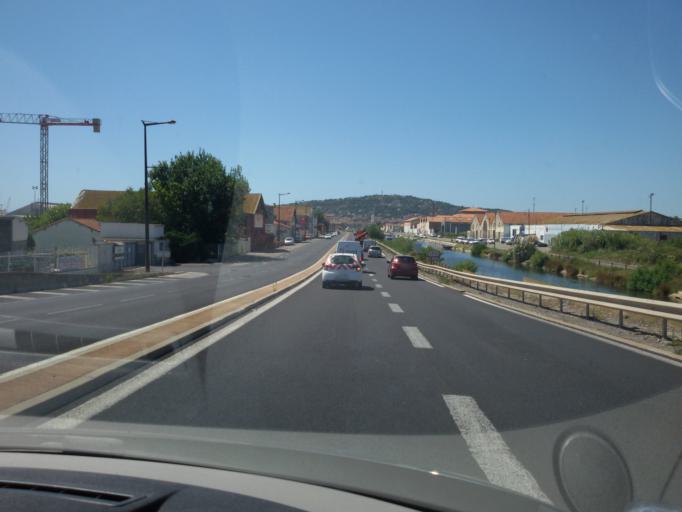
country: FR
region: Languedoc-Roussillon
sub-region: Departement de l'Herault
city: Sete
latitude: 43.4173
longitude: 3.7226
